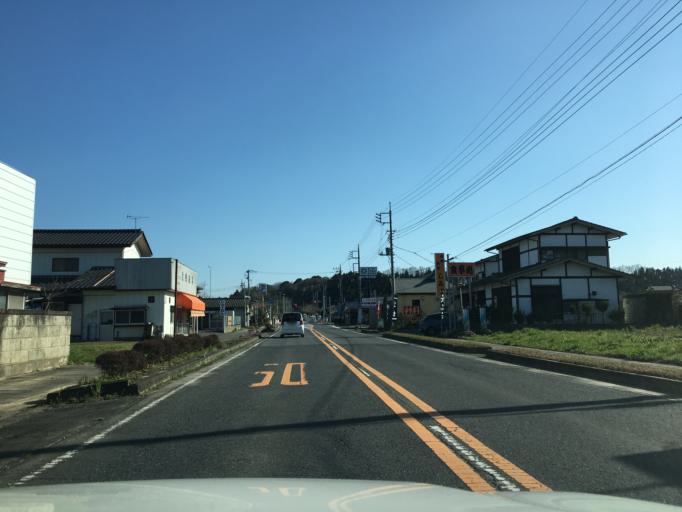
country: JP
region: Ibaraki
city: Omiya
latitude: 36.4458
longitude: 140.4107
